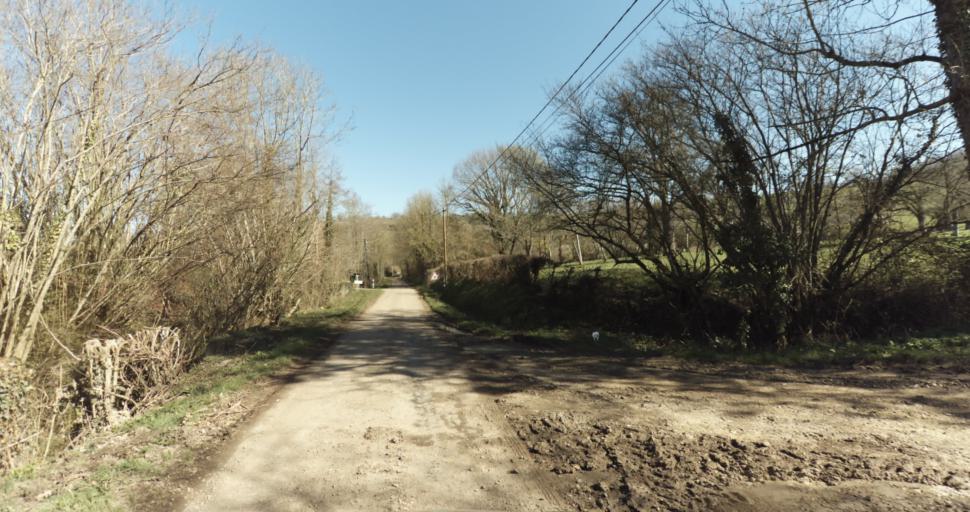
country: FR
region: Lower Normandy
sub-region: Departement du Calvados
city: Livarot
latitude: 48.9516
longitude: 0.0738
